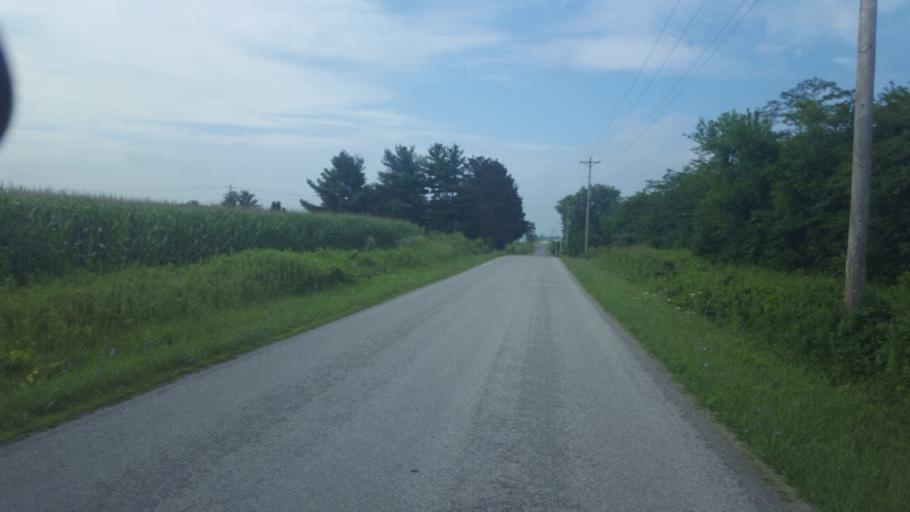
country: US
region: Ohio
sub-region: Delaware County
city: Ashley
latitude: 40.3947
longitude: -82.9115
